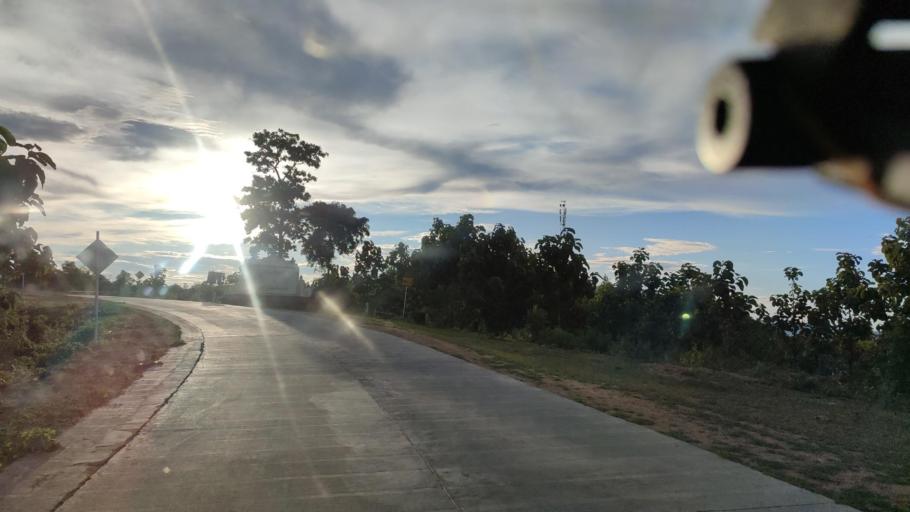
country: MM
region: Magway
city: Taungdwingyi
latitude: 20.0530
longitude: 95.7728
